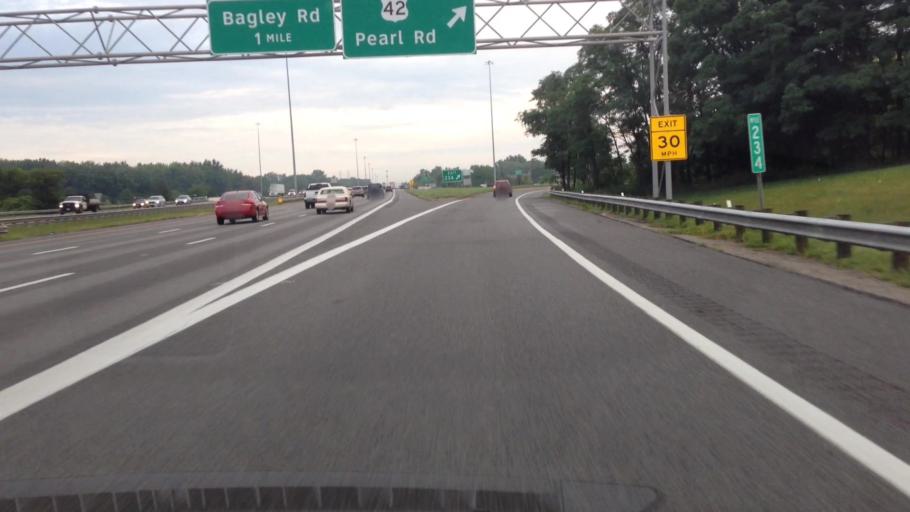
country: US
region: Ohio
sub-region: Cuyahoga County
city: Middleburg Heights
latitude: 41.3524
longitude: -81.8180
